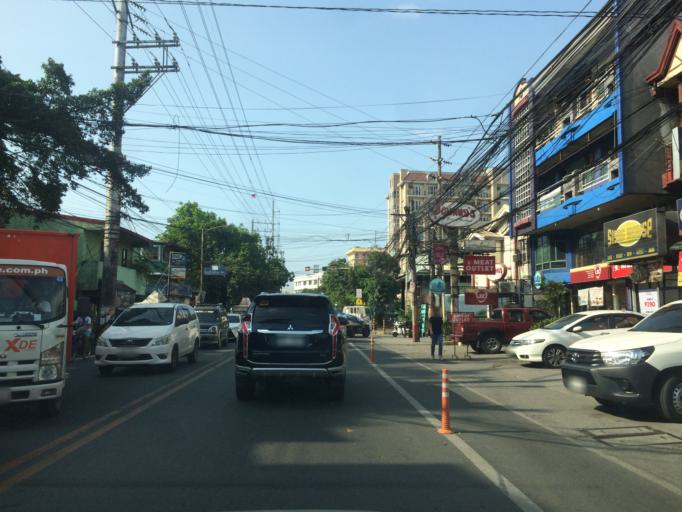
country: PH
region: Metro Manila
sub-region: Marikina
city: Calumpang
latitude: 14.6060
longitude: 121.0919
